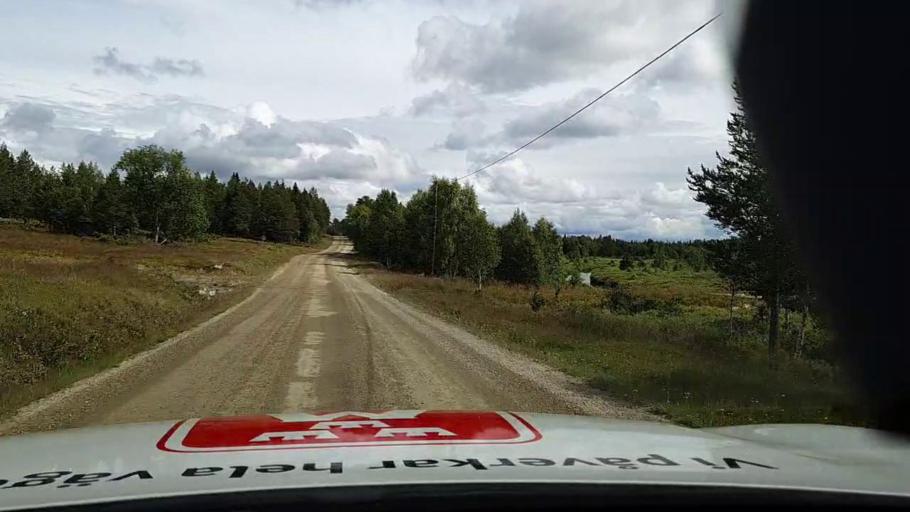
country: SE
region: Jaemtland
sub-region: Are Kommun
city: Jarpen
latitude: 62.5514
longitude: 13.4455
